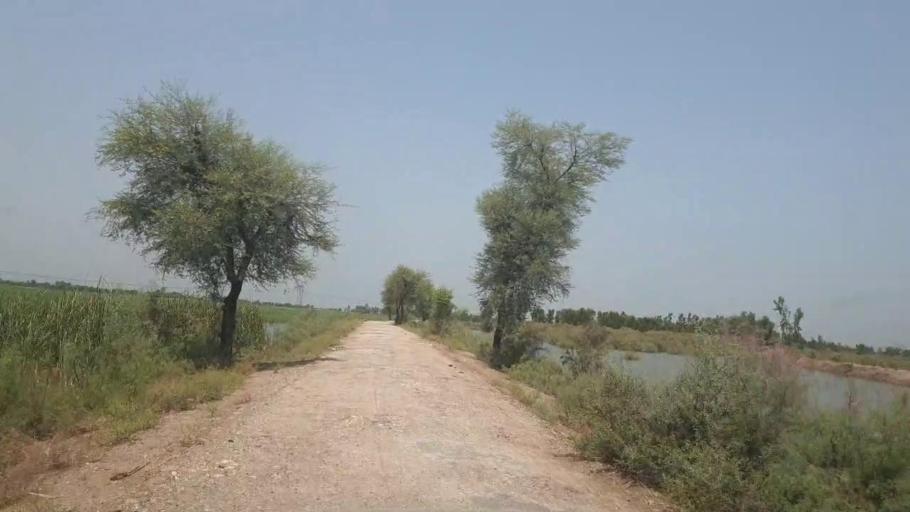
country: PK
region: Sindh
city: Lakhi
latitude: 27.8563
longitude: 68.6247
